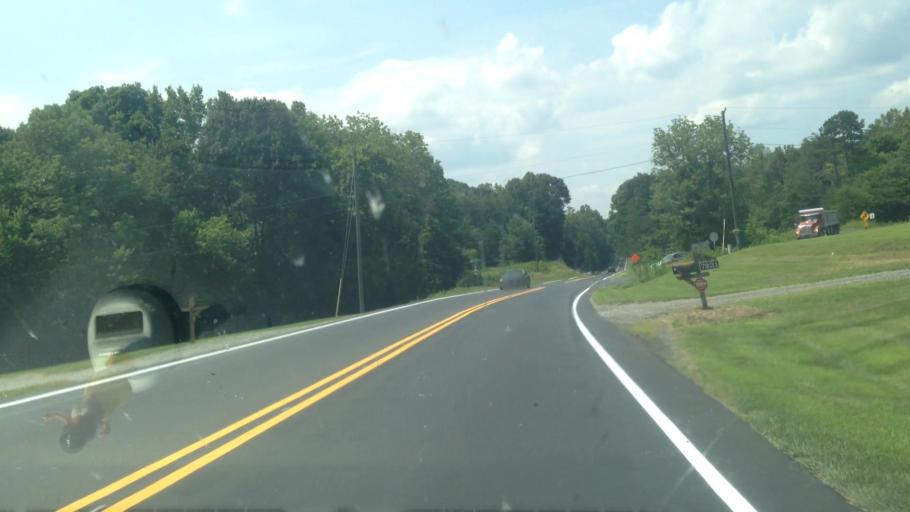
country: US
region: North Carolina
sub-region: Stokes County
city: Walnut Cove
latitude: 36.2512
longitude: -80.0985
